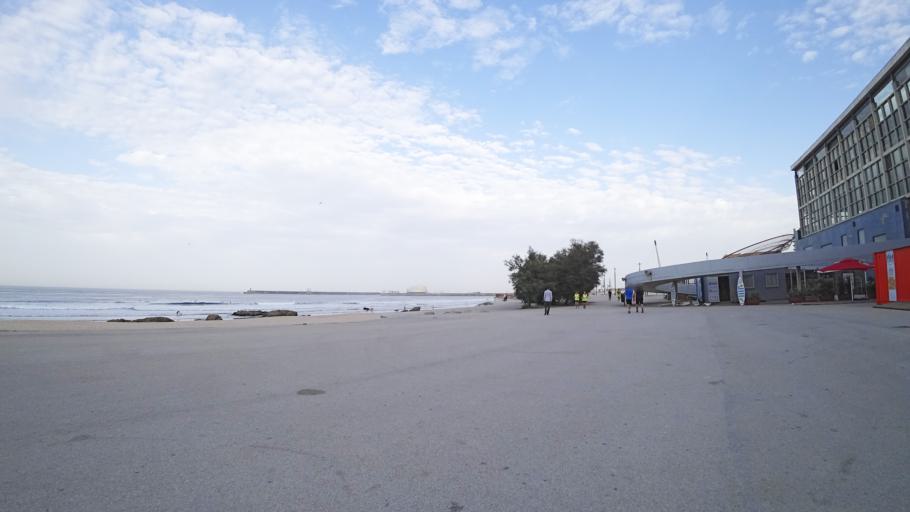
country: PT
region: Porto
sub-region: Matosinhos
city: Matosinhos
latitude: 41.1712
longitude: -8.6880
